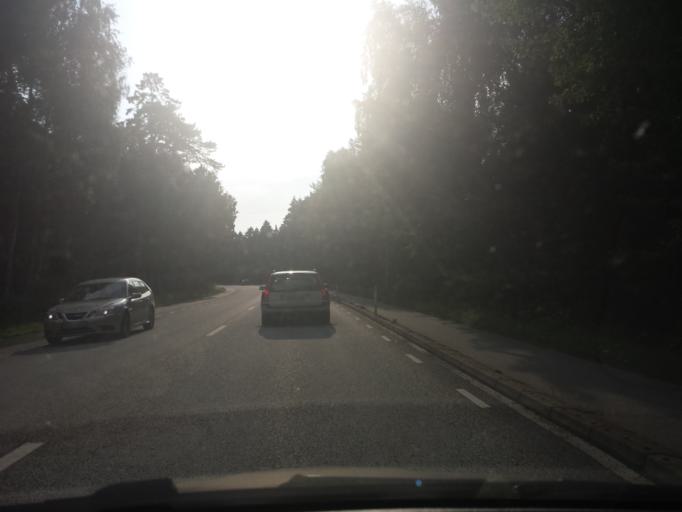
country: SE
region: Skane
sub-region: Ystads Kommun
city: Kopingebro
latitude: 55.4363
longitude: 13.8905
